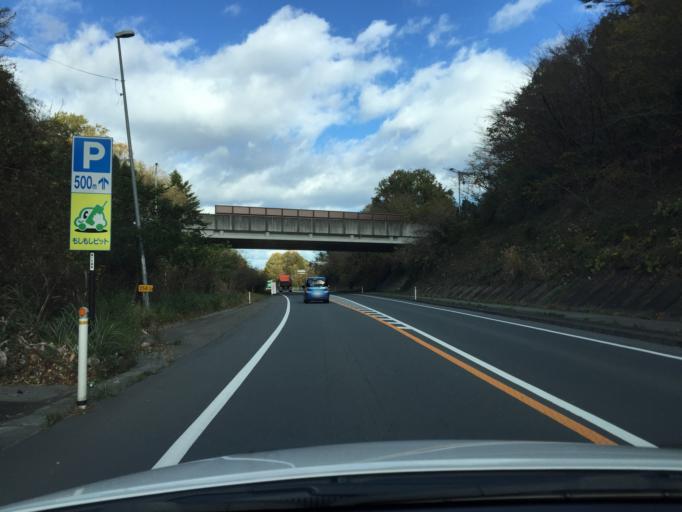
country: JP
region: Fukushima
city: Namie
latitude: 37.4366
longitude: 141.0113
